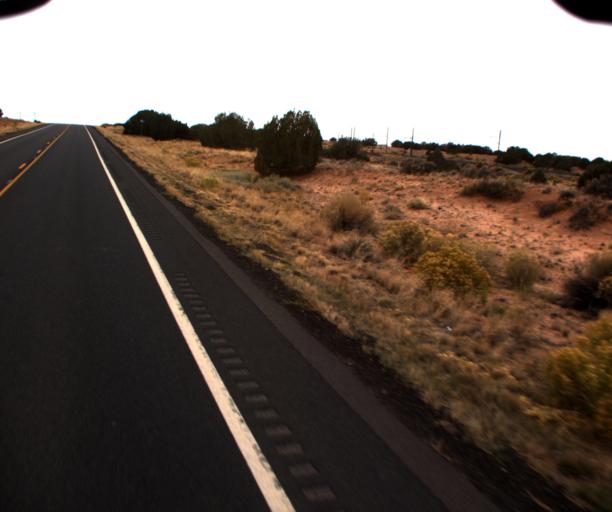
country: US
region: Arizona
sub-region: Coconino County
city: Kaibito
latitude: 36.4437
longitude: -110.7336
